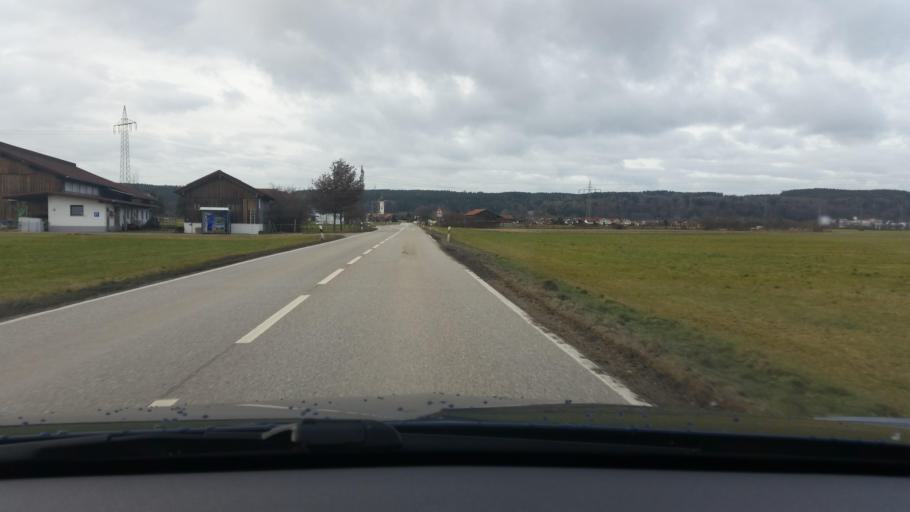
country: DE
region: Bavaria
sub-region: Upper Bavaria
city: Wolfratshausen
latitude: 47.8922
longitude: 11.4389
